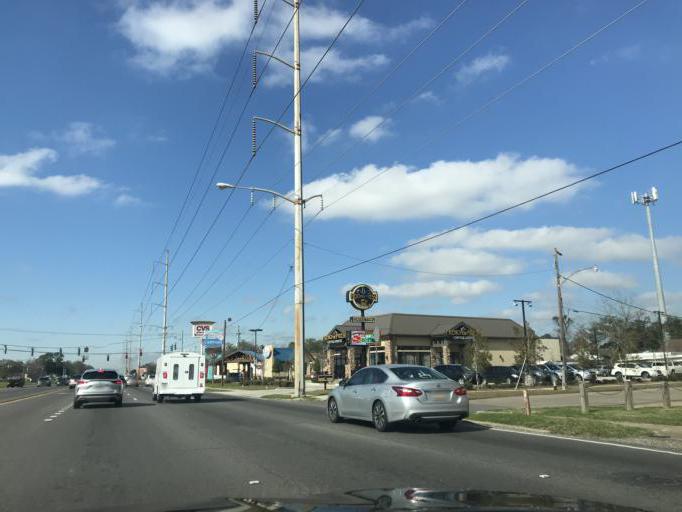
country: US
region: Louisiana
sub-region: Jefferson Parish
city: Metairie Terrace
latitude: 29.9754
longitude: -90.1737
